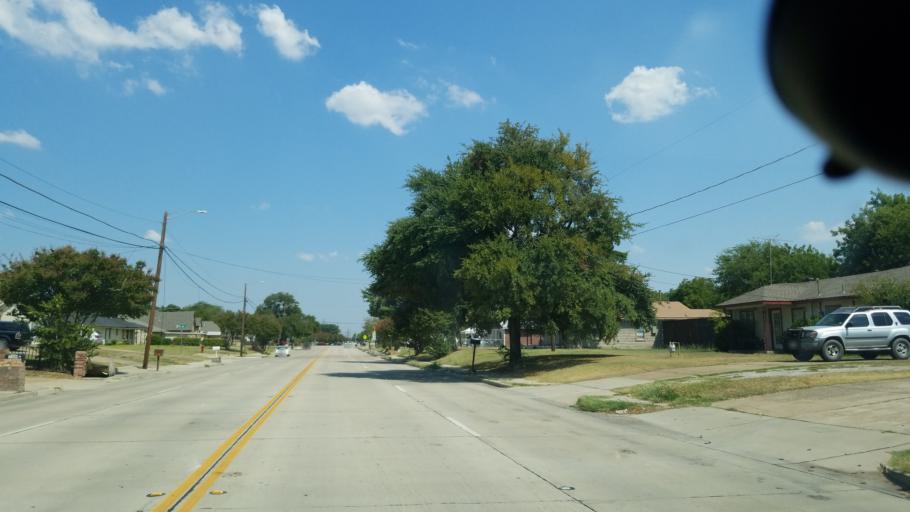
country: US
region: Texas
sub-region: Dallas County
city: Grand Prairie
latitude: 32.7145
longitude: -96.9861
